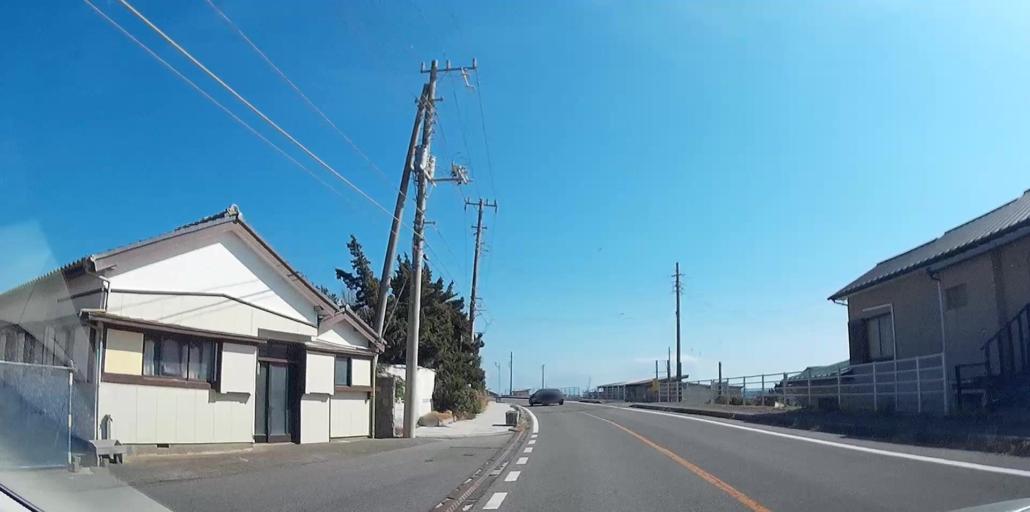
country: JP
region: Chiba
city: Tateyama
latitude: 34.9047
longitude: 139.8709
